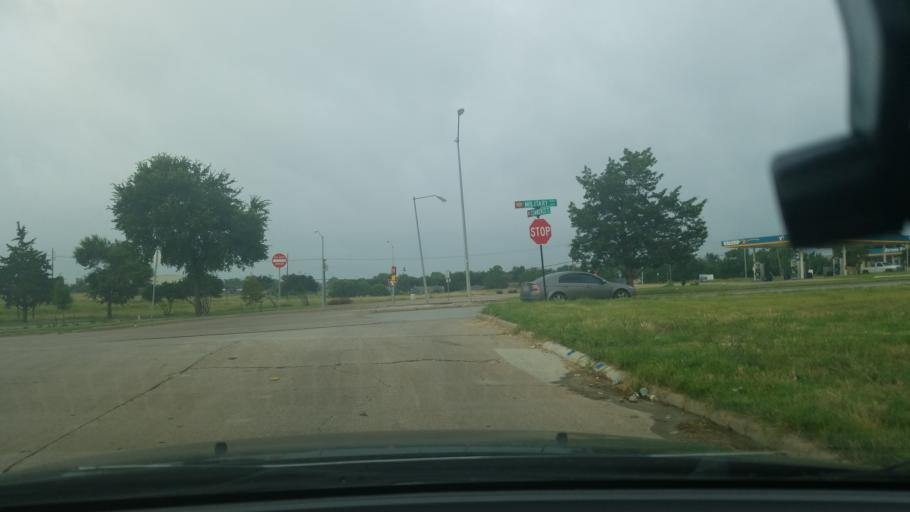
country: US
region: Texas
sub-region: Dallas County
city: Mesquite
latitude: 32.7684
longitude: -96.6270
